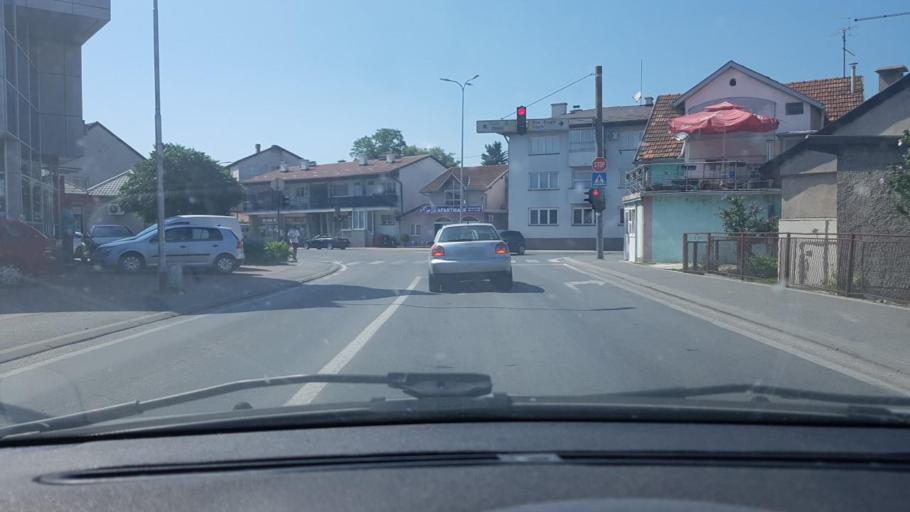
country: BA
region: Federation of Bosnia and Herzegovina
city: Bihac
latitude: 44.8143
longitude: 15.8778
